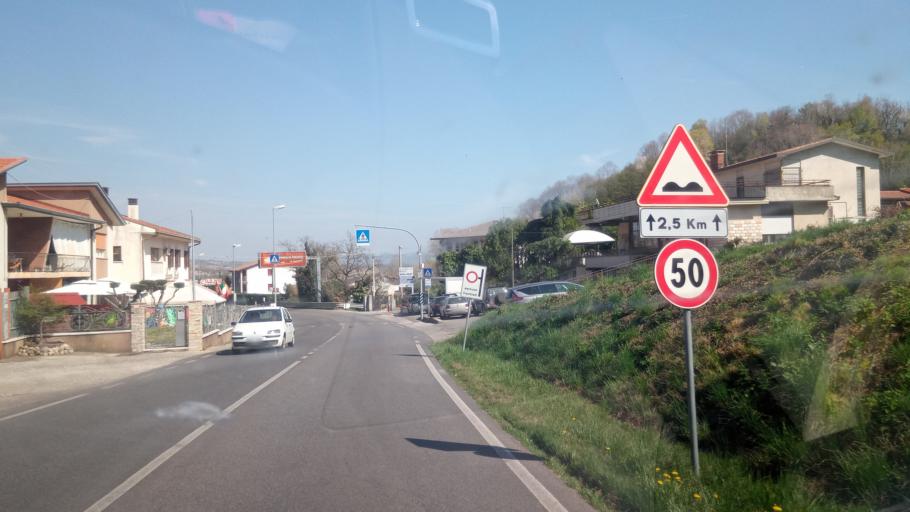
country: IT
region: Veneto
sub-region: Provincia di Treviso
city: Borso del Grappa
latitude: 45.8029
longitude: 11.7663
